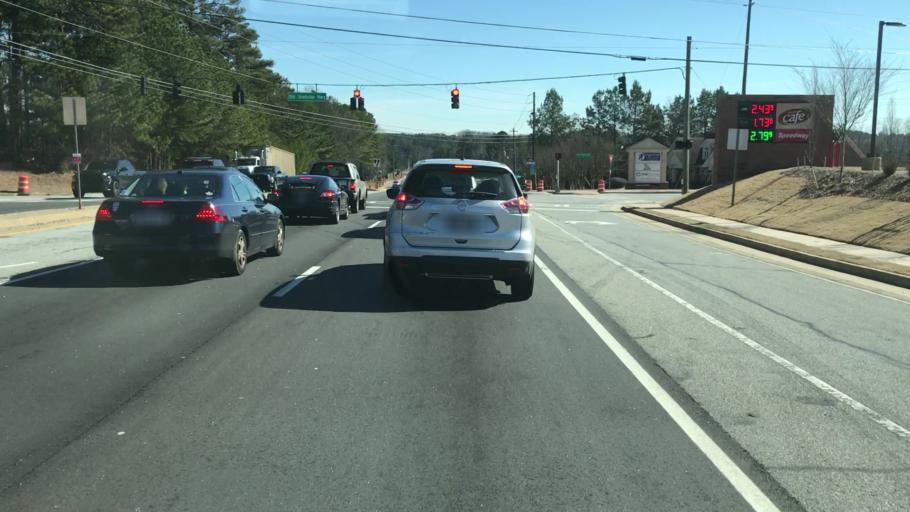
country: US
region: Georgia
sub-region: Gwinnett County
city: Lawrenceville
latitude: 33.9200
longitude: -84.0062
